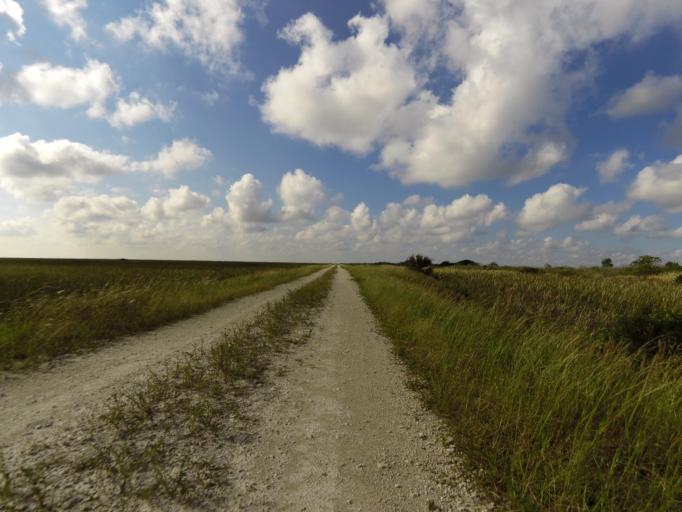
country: US
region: Florida
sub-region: Broward County
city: Weston
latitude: 26.0467
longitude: -80.4833
